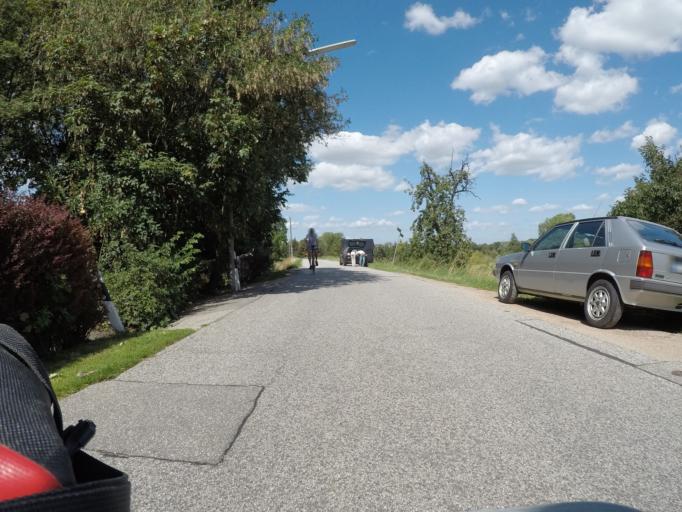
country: DE
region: Hamburg
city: Rothenburgsort
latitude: 53.4807
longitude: 10.0873
